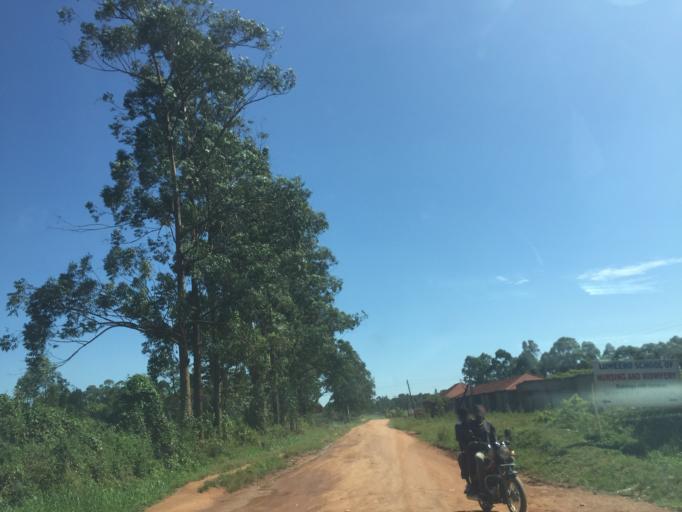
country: UG
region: Central Region
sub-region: Luwero District
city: Luwero
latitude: 0.8447
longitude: 32.5091
